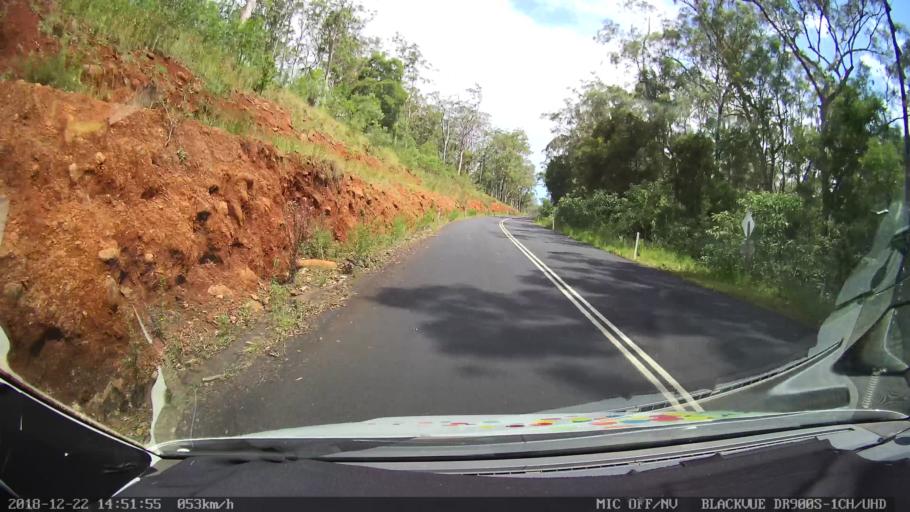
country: AU
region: New South Wales
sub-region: Bellingen
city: Dorrigo
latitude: -30.2057
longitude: 152.5436
